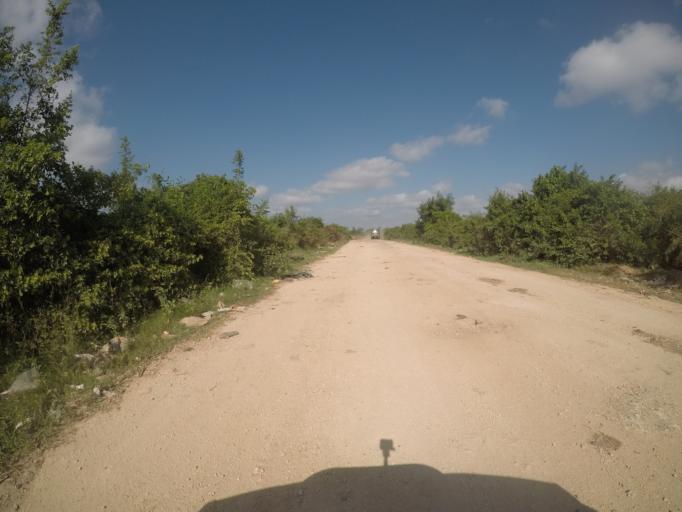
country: TZ
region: Zanzibar Central/South
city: Koani
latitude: -6.2189
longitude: 39.3282
